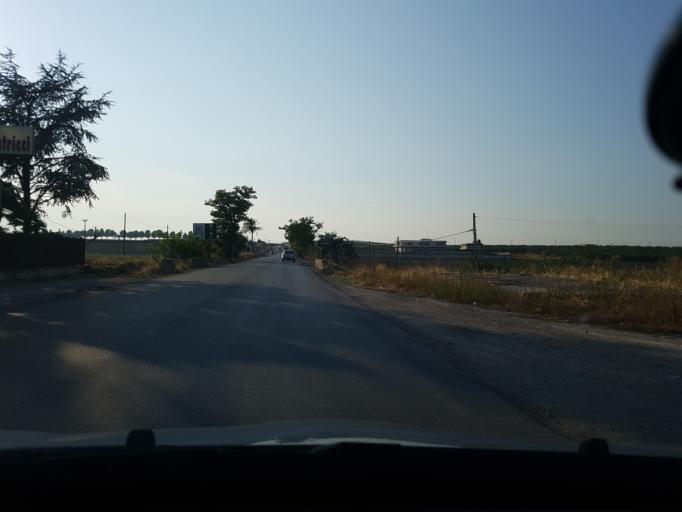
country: IT
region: Apulia
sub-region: Provincia di Foggia
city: Cerignola
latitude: 41.2698
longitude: 15.8814
